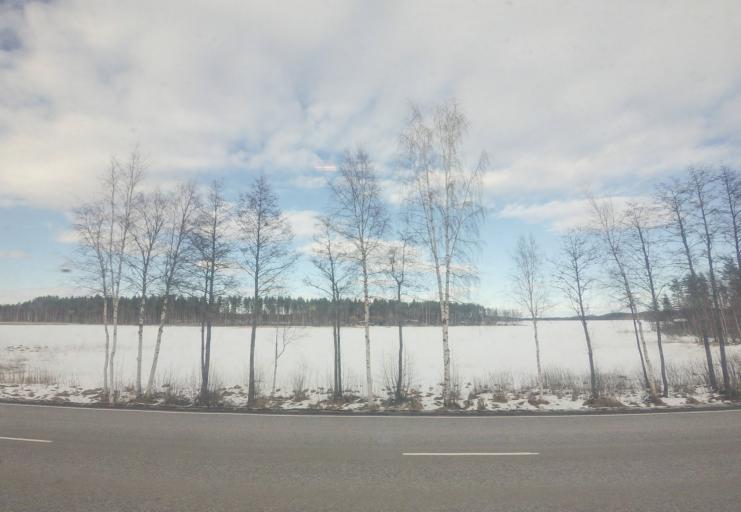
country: FI
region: Southern Savonia
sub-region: Savonlinna
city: Kerimaeki
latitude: 61.8172
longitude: 29.2589
